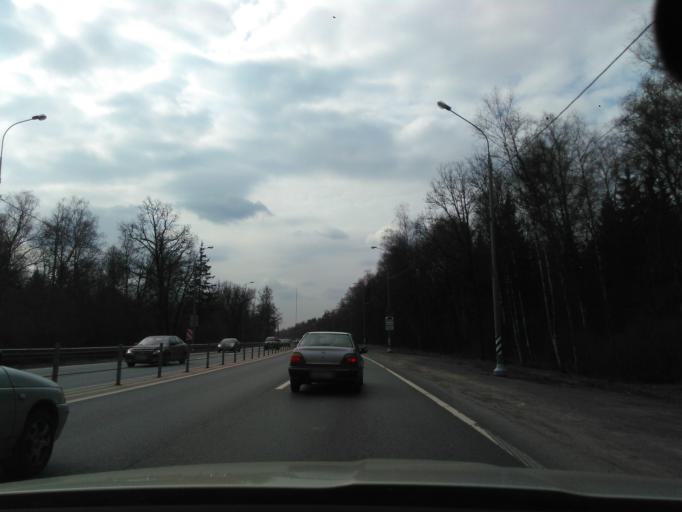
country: RU
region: Moskovskaya
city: Marfino
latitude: 56.0325
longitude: 37.5424
